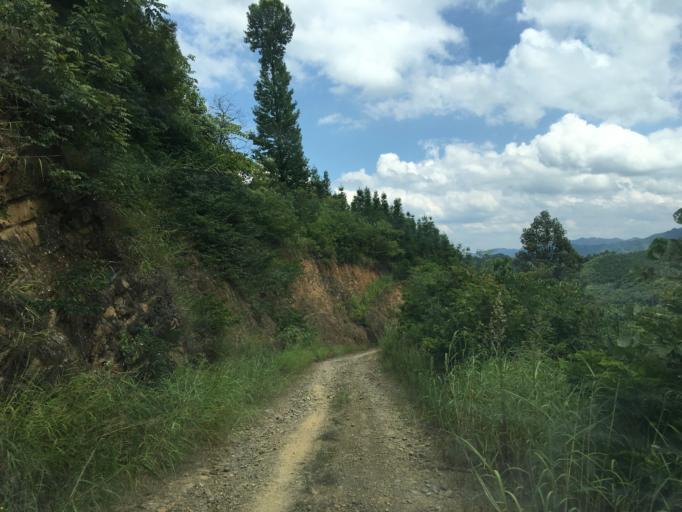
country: CN
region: Guangxi Zhuangzu Zizhiqu
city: Tongle
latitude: 24.9711
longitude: 105.9743
